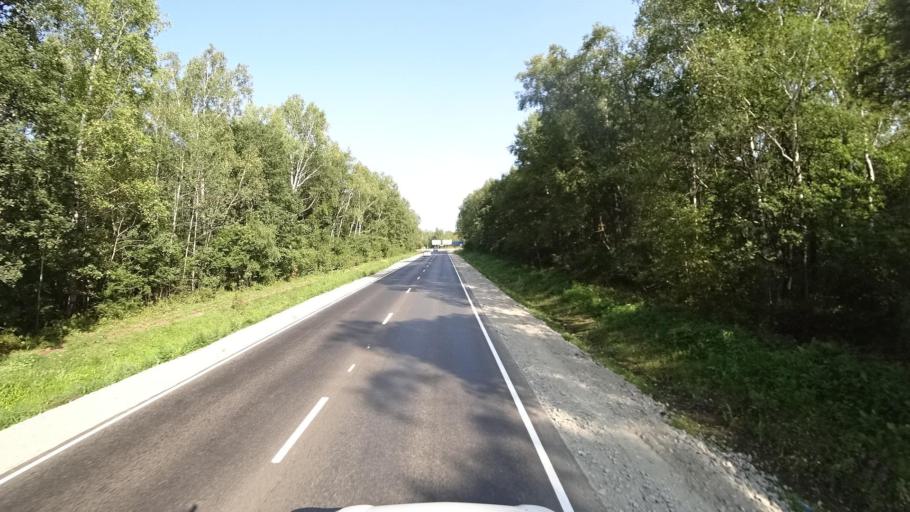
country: RU
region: Khabarovsk Krai
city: Khor
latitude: 47.9755
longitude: 135.0799
